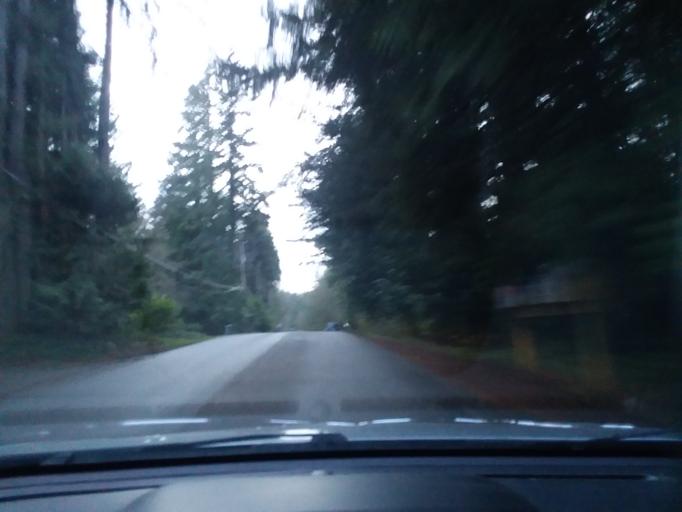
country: US
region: Washington
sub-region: King County
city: Lake Forest Park
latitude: 47.7609
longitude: -122.2940
